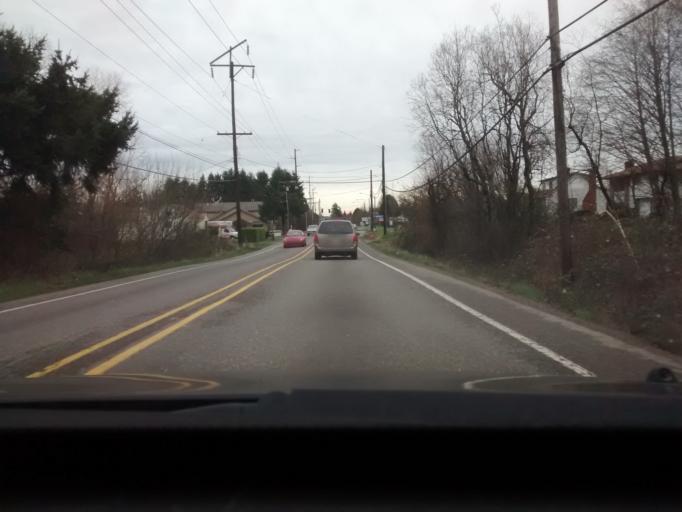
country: US
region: Washington
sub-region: Kitsap County
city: East Port Orchard
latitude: 47.5145
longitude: -122.6313
